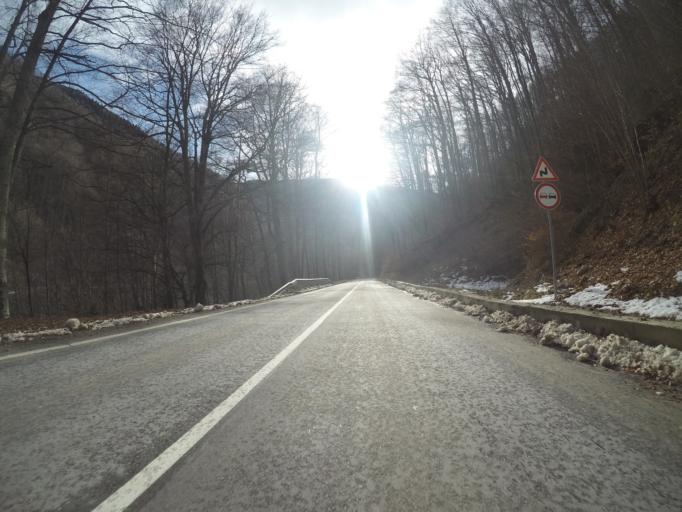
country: BG
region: Kyustendil
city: Sapareva Banya
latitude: 42.1214
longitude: 23.3273
